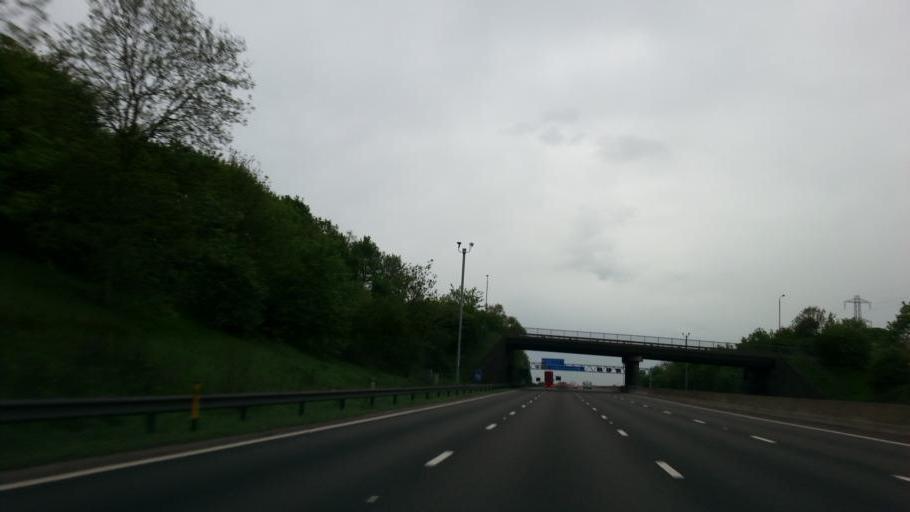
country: GB
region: England
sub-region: Derbyshire
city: Staveley
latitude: 53.2354
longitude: -1.3330
